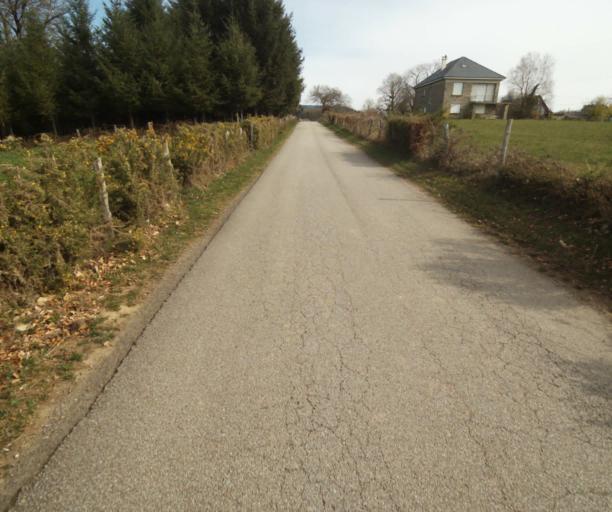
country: FR
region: Limousin
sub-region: Departement de la Correze
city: Correze
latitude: 45.4229
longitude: 1.8317
